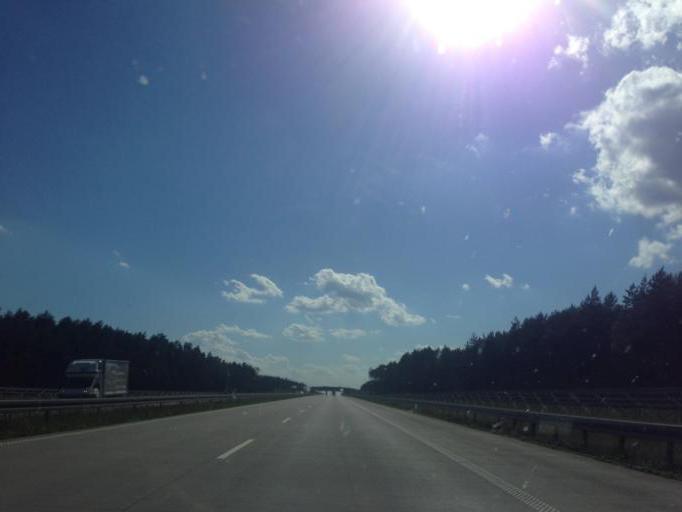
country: PL
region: Lower Silesian Voivodeship
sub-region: Powiat boleslawiecki
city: Boleslawiec
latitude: 51.2841
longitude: 15.4737
